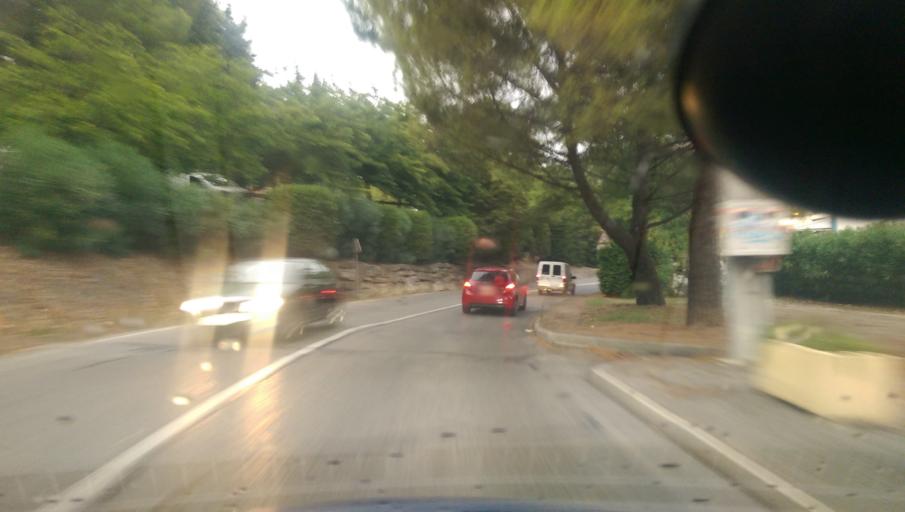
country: FR
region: Provence-Alpes-Cote d'Azur
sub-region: Departement des Alpes-Maritimes
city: Opio
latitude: 43.6764
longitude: 6.9753
